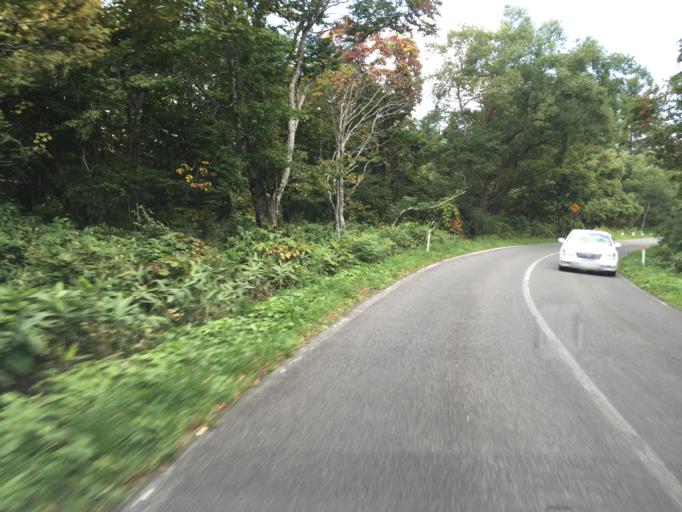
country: JP
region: Fukushima
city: Inawashiro
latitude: 37.6210
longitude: 140.0531
